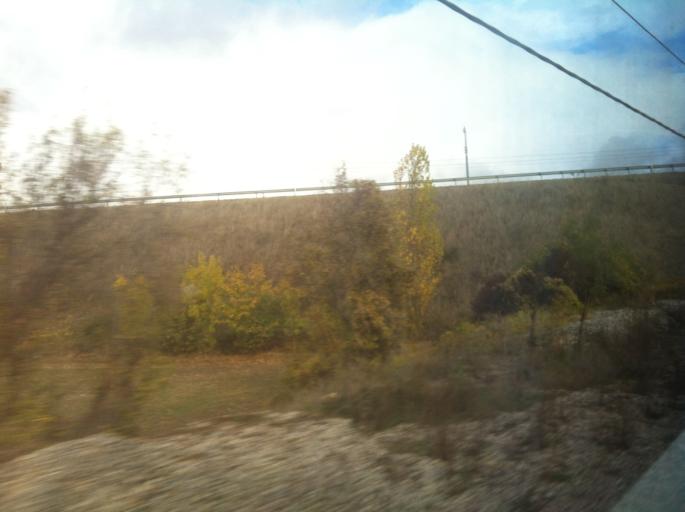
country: ES
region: Basque Country
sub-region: Provincia de Alava
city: Arminon
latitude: 42.8118
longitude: -2.8171
